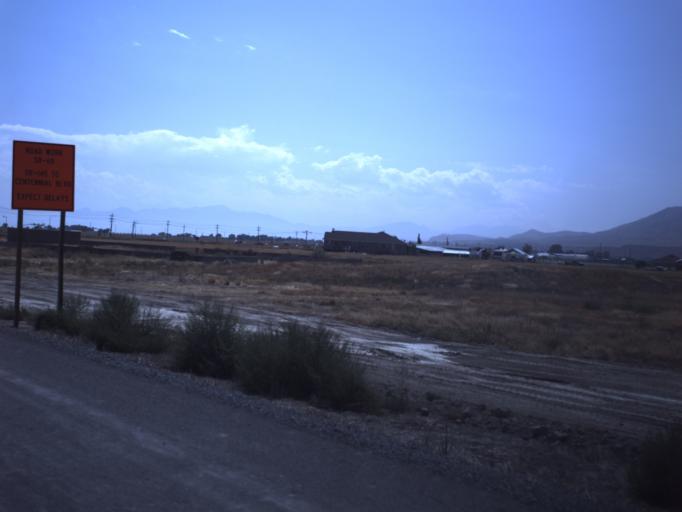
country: US
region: Utah
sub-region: Utah County
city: Saratoga Springs
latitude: 40.3733
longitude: -111.9207
